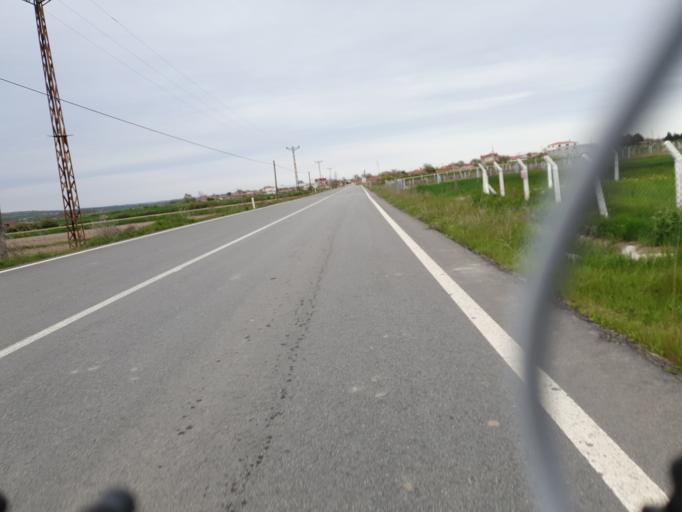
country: TR
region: Tekirdag
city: Saray
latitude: 41.3659
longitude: 27.8588
